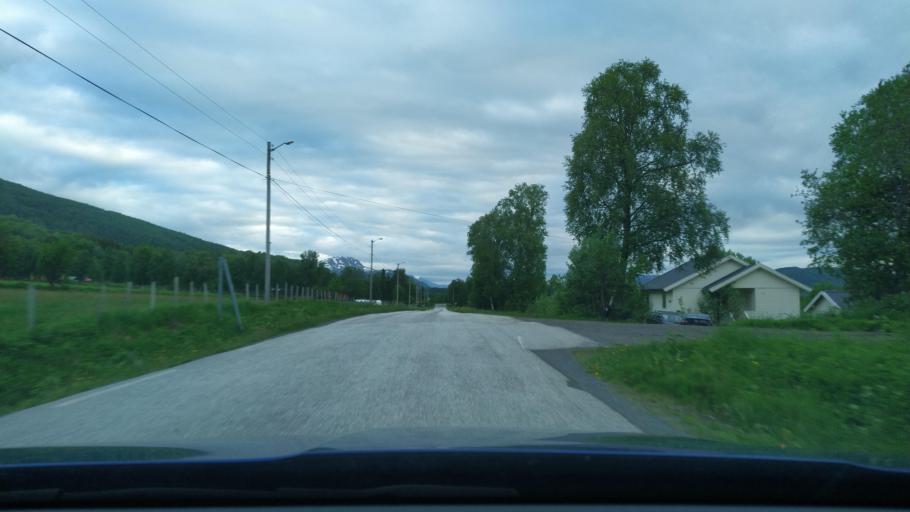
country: NO
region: Troms
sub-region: Tranoy
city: Vangsvika
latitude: 69.1191
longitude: 17.8069
